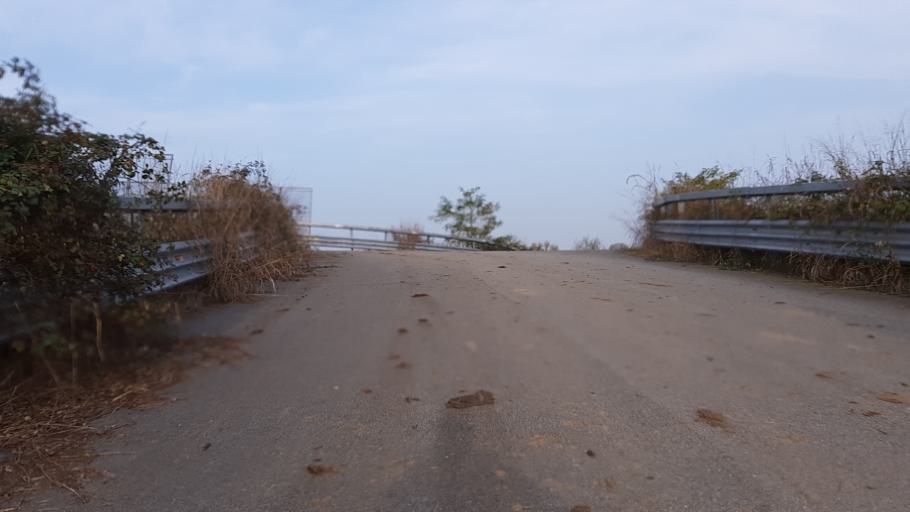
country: IT
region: Piedmont
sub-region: Provincia di Torino
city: Settimo Torinese
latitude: 45.1288
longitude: 7.7229
